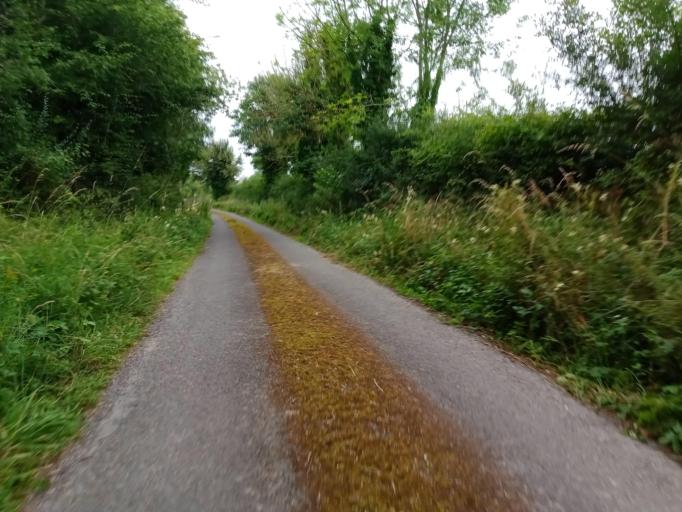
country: IE
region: Leinster
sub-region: Kilkenny
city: Callan
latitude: 52.5365
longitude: -7.4205
